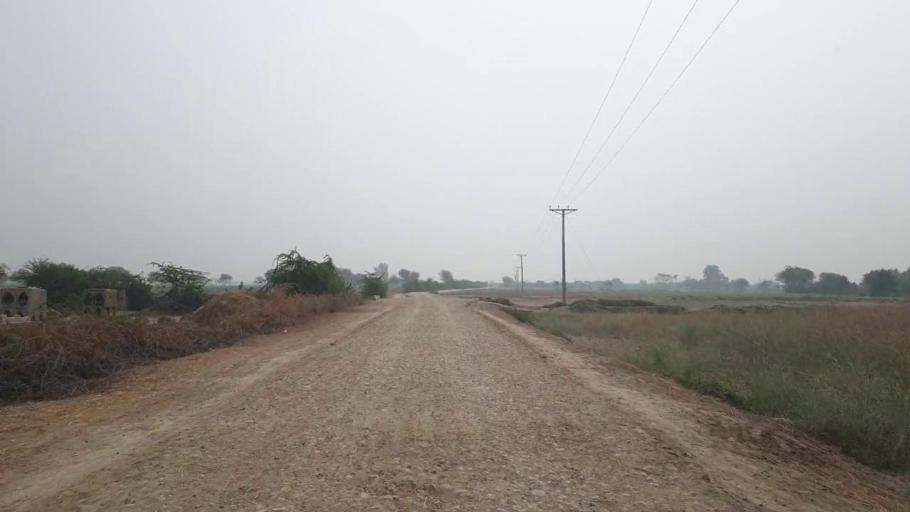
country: PK
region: Sindh
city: Kario
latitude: 24.6404
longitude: 68.6406
